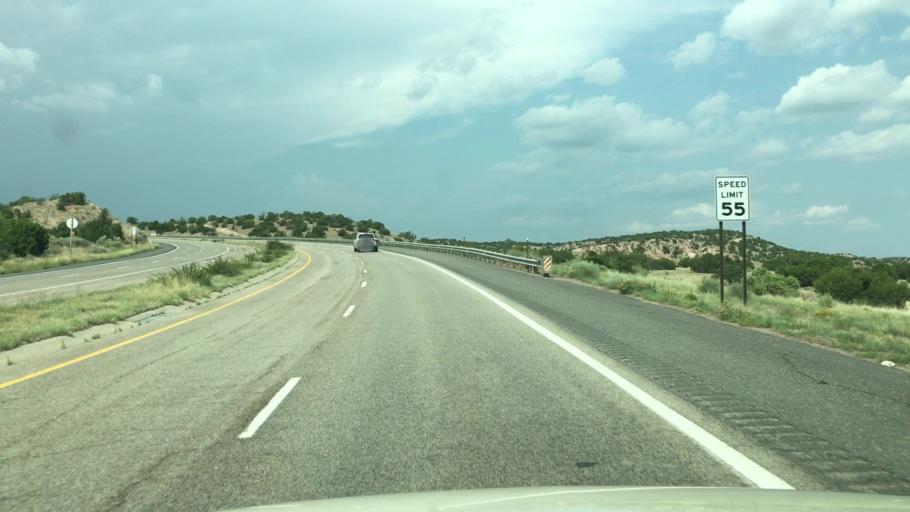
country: US
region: New Mexico
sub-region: Santa Fe County
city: Eldorado at Santa Fe
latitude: 35.4852
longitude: -105.9046
